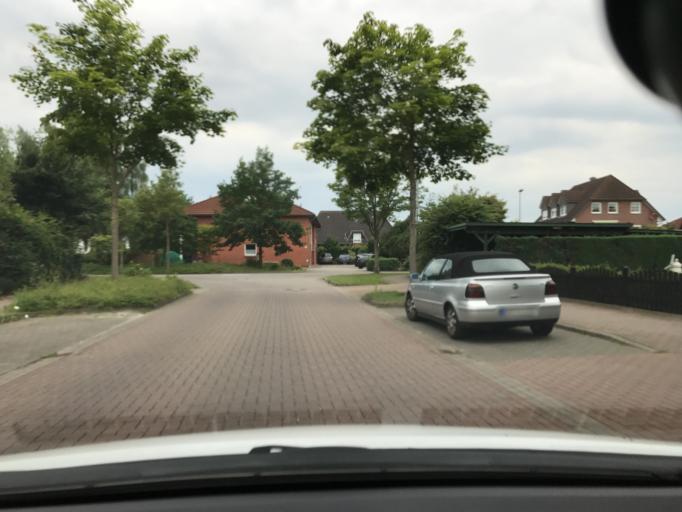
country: DE
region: Lower Saxony
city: Syke
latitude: 52.9901
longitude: 8.8642
